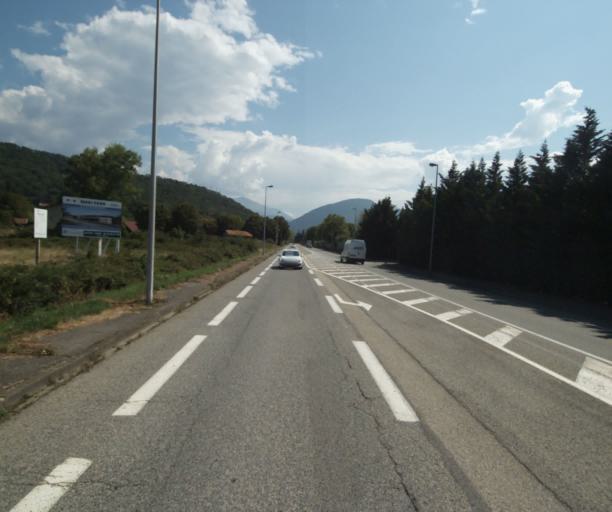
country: FR
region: Rhone-Alpes
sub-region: Departement de l'Isere
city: Le Pont-de-Claix
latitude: 45.1180
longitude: 5.7026
